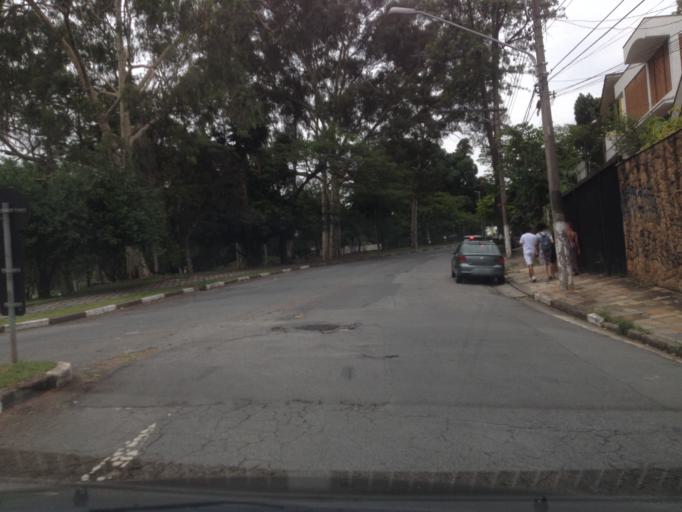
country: BR
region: Sao Paulo
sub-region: Sao Paulo
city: Sao Paulo
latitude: -23.5519
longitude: -46.6857
